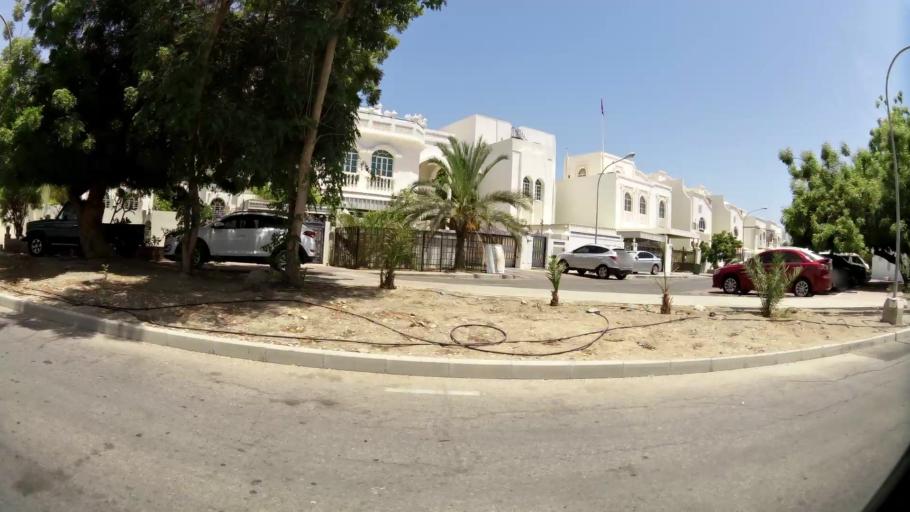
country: OM
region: Muhafazat Masqat
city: Bawshar
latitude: 23.6097
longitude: 58.4576
